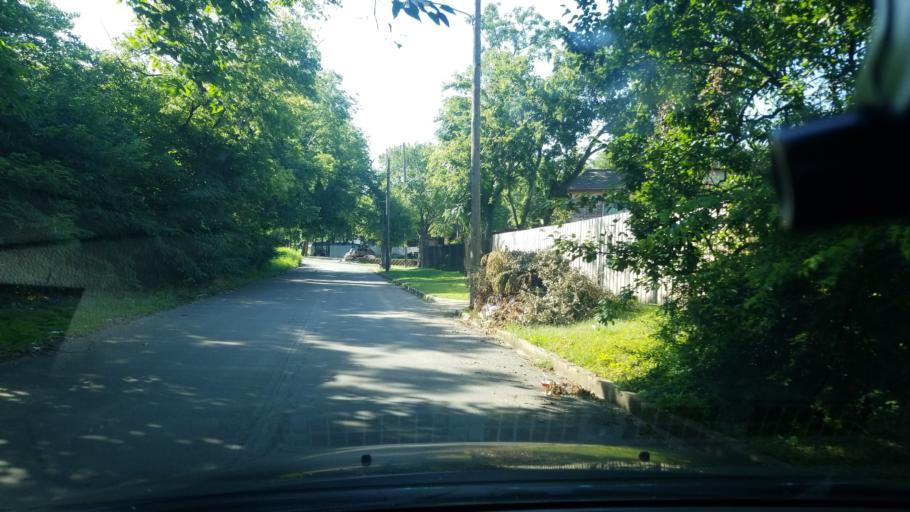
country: US
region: Texas
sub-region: Dallas County
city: Dallas
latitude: 32.7265
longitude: -96.8239
